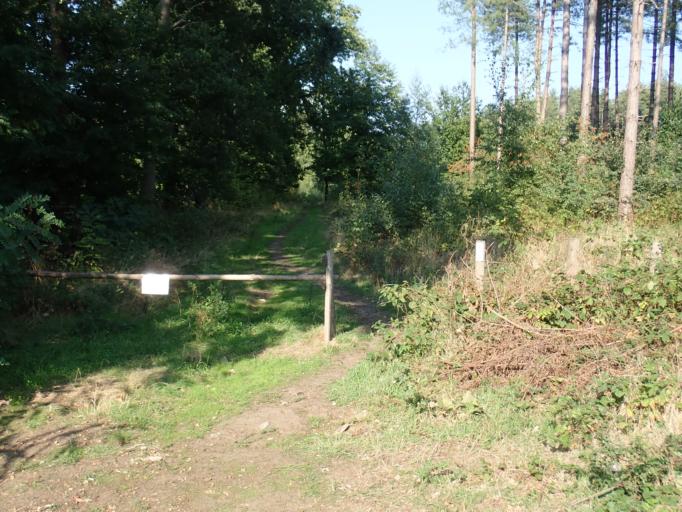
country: BE
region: Flanders
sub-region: Provincie Vlaams-Brabant
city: Scherpenheuvel-Zichem
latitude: 51.0251
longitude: 4.9553
